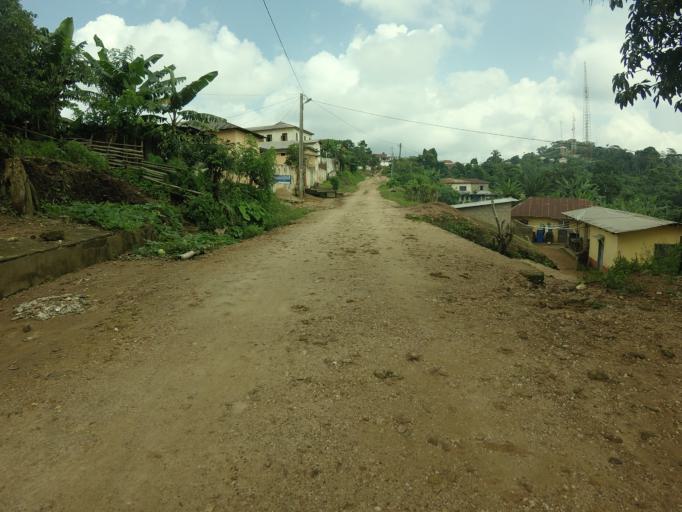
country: TG
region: Plateaux
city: Kpalime
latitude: 6.8464
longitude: 0.4358
